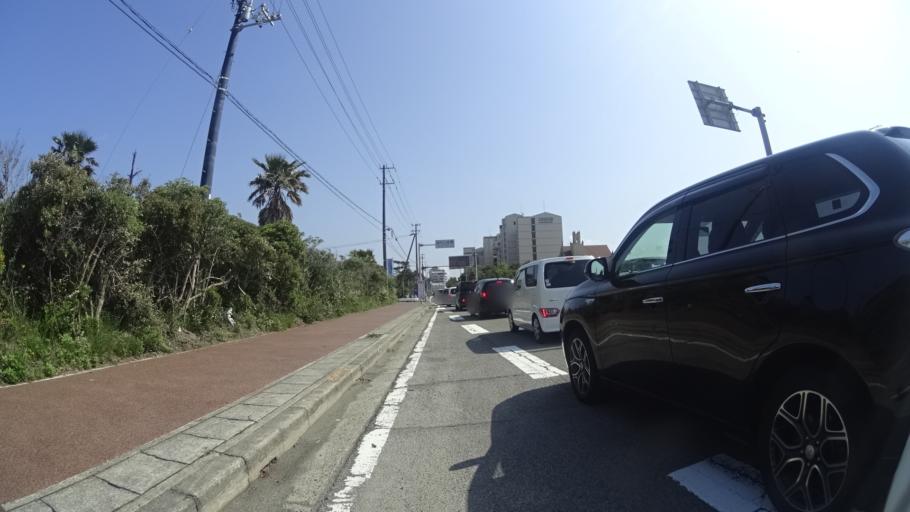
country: JP
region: Tokushima
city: Narutocho-mitsuishi
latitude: 34.2183
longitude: 134.6311
